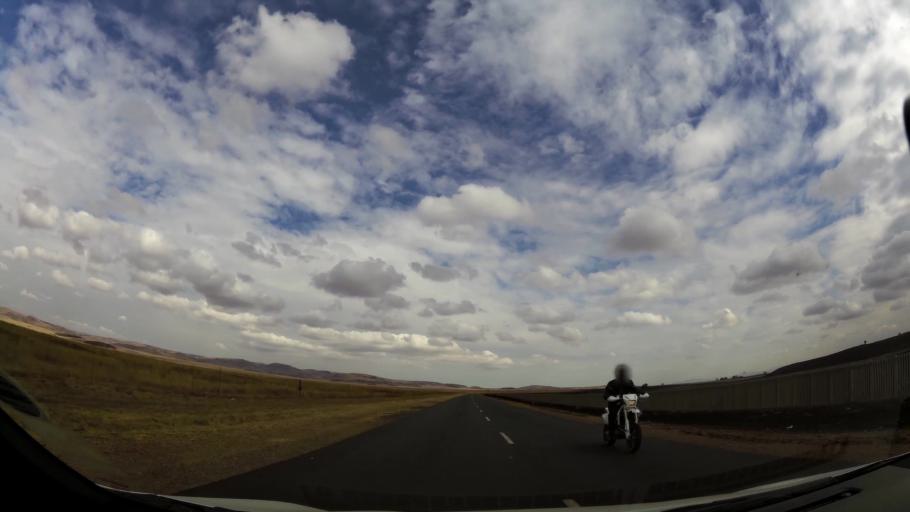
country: ZA
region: Gauteng
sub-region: Sedibeng District Municipality
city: Heidelberg
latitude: -26.4325
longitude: 28.2561
